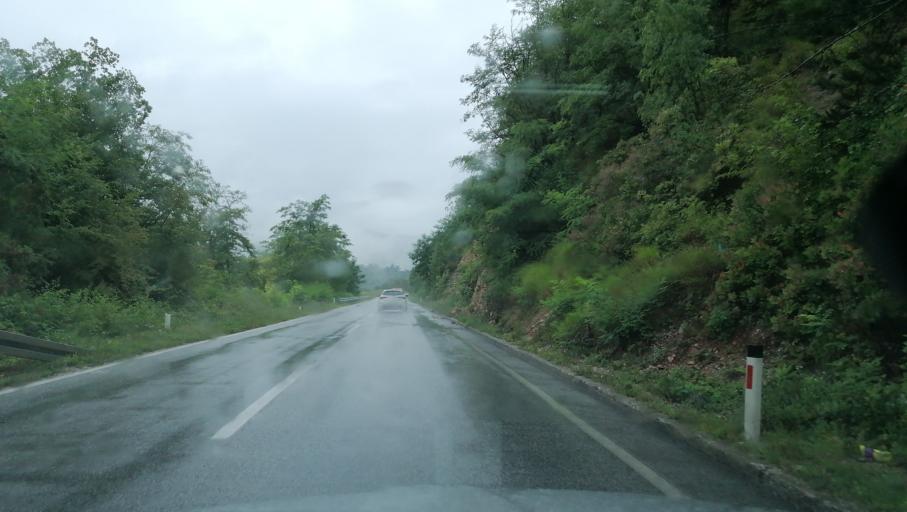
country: BA
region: Federation of Bosnia and Herzegovina
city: Gorazde
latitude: 43.6796
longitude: 19.0665
